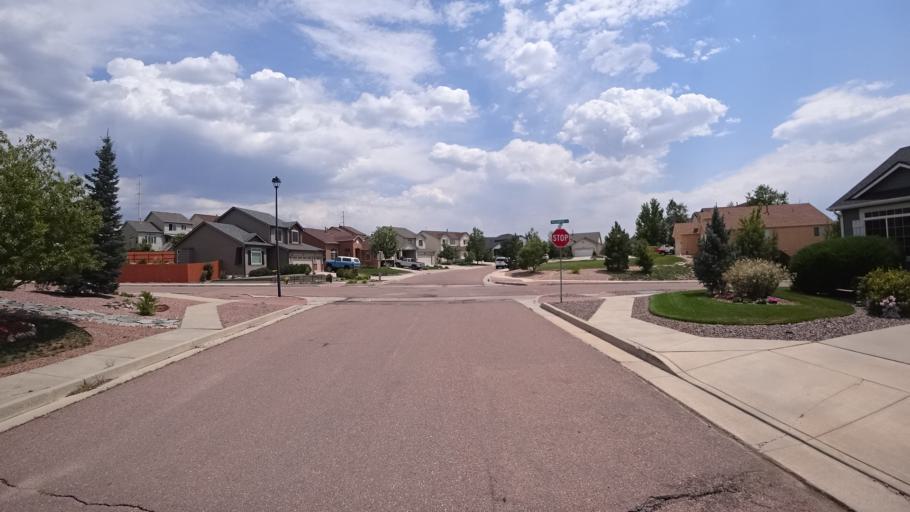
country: US
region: Colorado
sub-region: El Paso County
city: Black Forest
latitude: 38.9638
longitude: -104.7404
